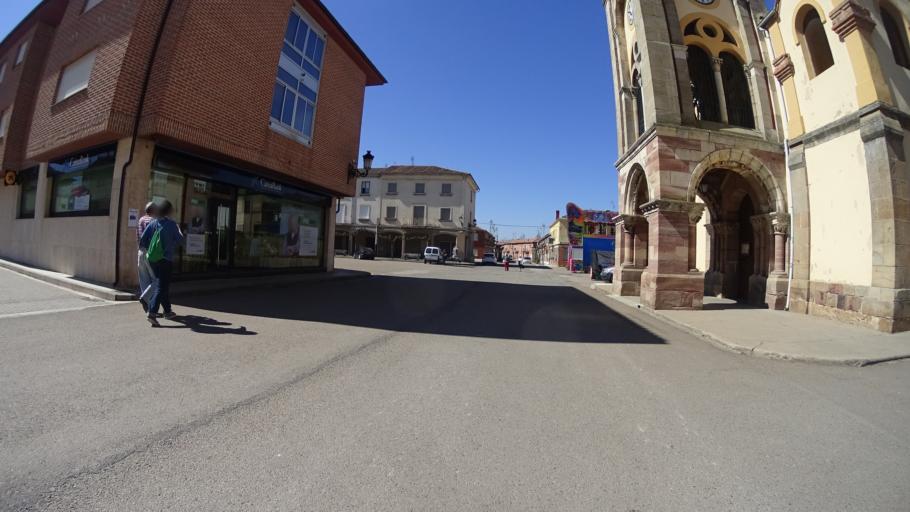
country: ES
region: Castille and Leon
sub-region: Provincia de Palencia
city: Alar del Rey
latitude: 42.6599
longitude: -4.3110
